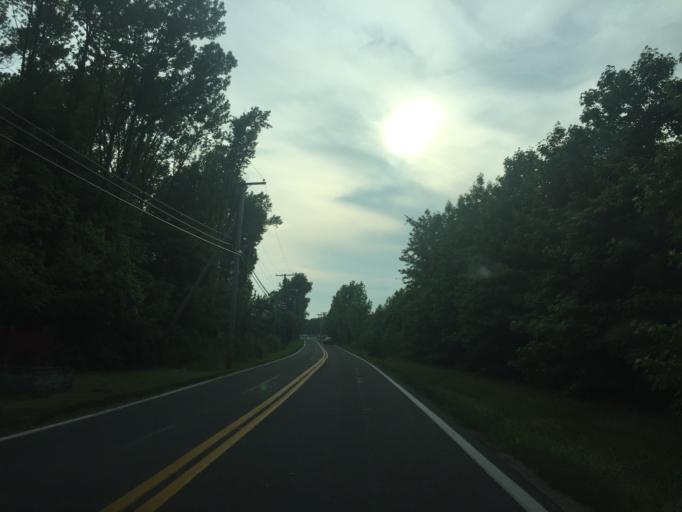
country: US
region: Maryland
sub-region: Baltimore County
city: Edgemere
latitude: 39.2291
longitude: -76.4273
